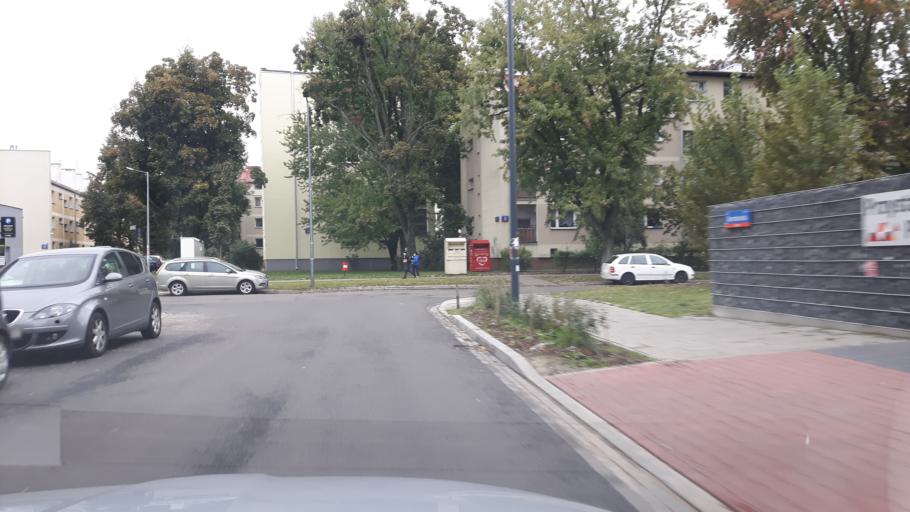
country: PL
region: Masovian Voivodeship
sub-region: Warszawa
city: Praga Poludnie
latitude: 52.2495
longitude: 21.0991
